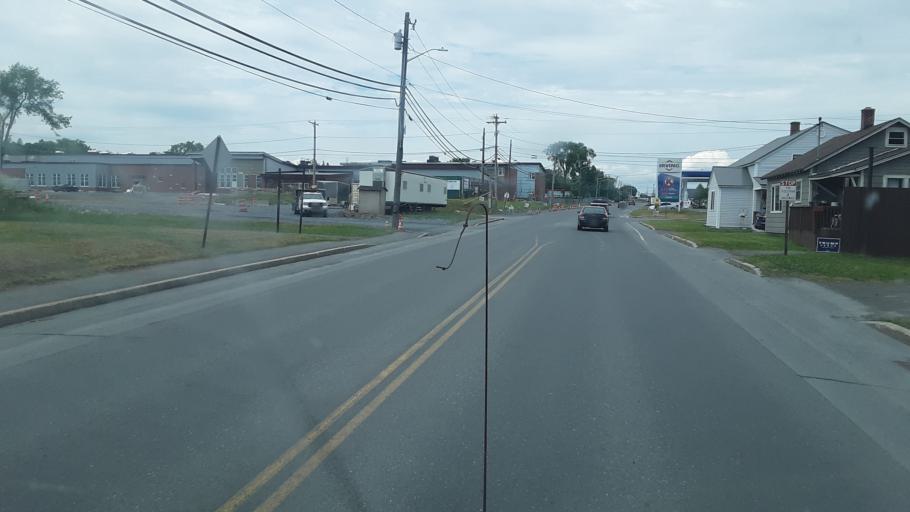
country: US
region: Maine
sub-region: Aroostook County
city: Caribou
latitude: 46.8618
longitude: -68.0047
